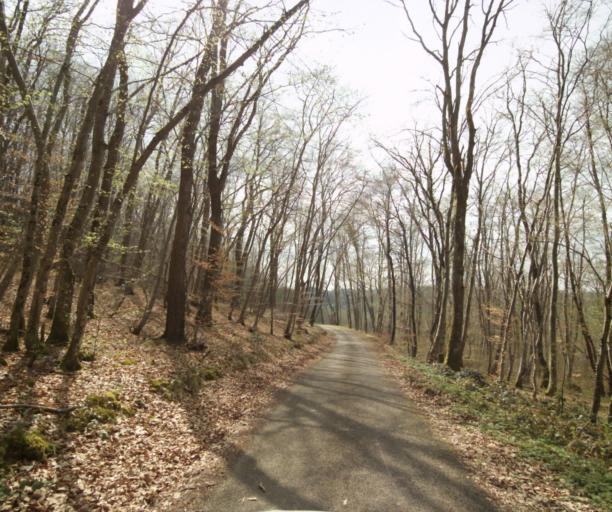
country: FR
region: Bourgogne
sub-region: Departement de Saone-et-Loire
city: Charolles
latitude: 46.3877
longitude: 4.2716
